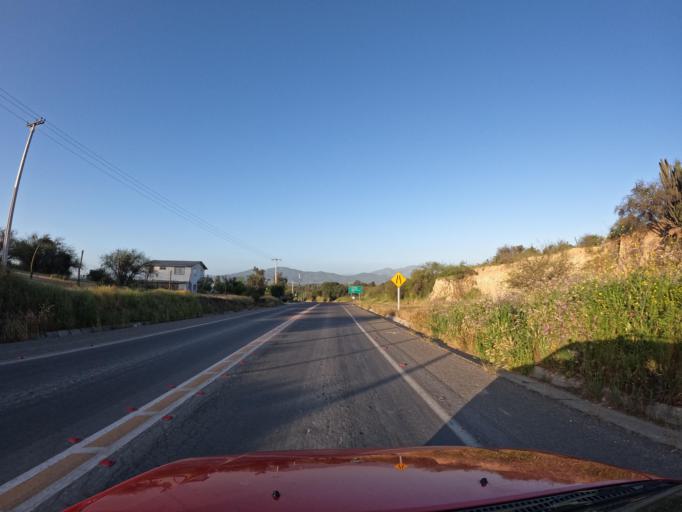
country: CL
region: O'Higgins
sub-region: Provincia de Colchagua
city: Santa Cruz
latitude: -34.3185
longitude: -71.3878
